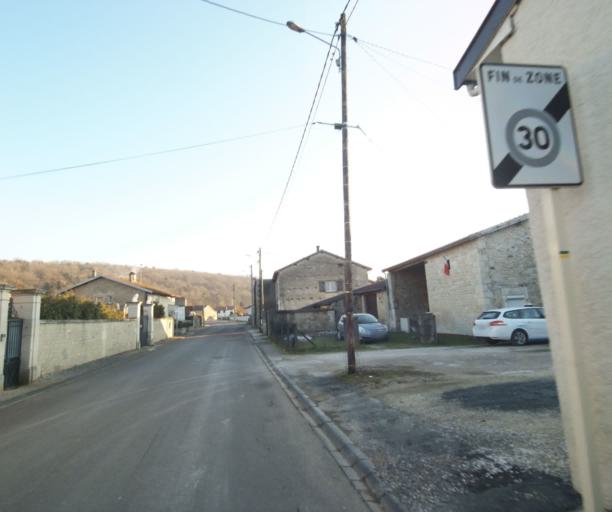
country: FR
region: Champagne-Ardenne
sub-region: Departement de la Haute-Marne
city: Chevillon
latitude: 48.5390
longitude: 5.1046
